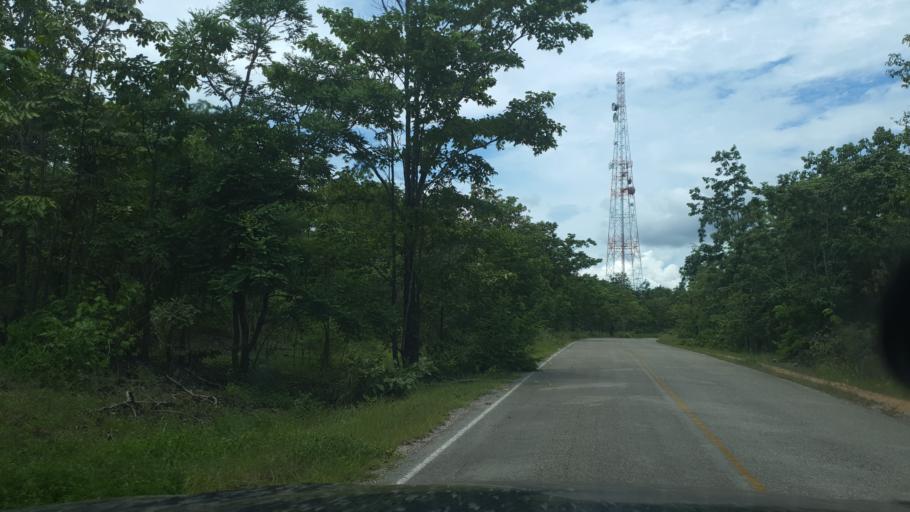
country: TH
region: Lampang
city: Soem Ngam
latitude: 18.0387
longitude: 99.3743
